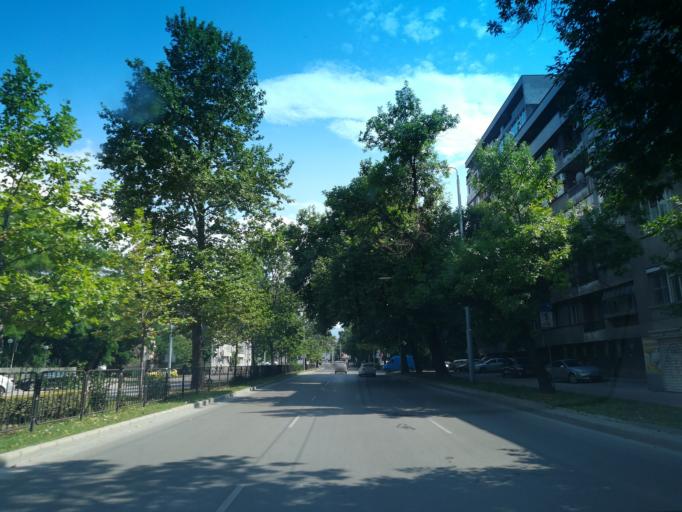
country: BG
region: Plovdiv
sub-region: Obshtina Plovdiv
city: Plovdiv
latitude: 42.1382
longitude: 24.7629
